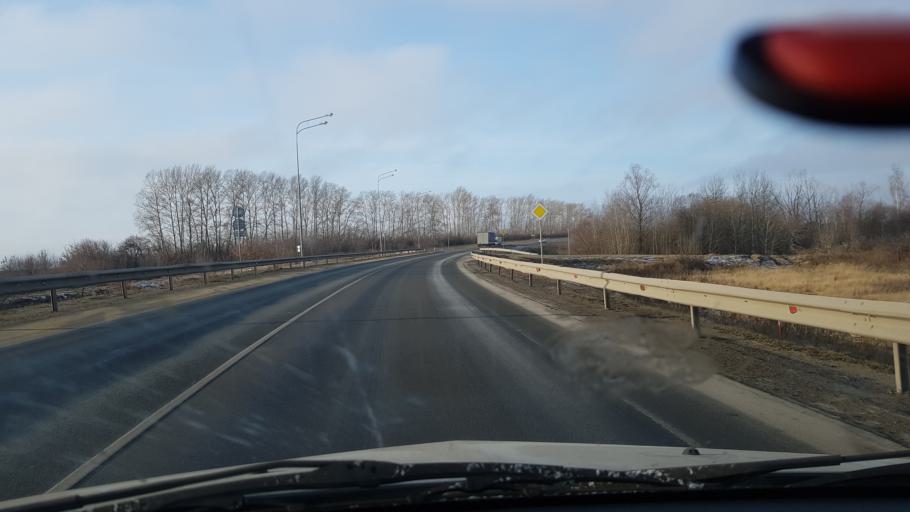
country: RU
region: Tatarstan
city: Laishevo
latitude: 55.3914
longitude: 49.7954
